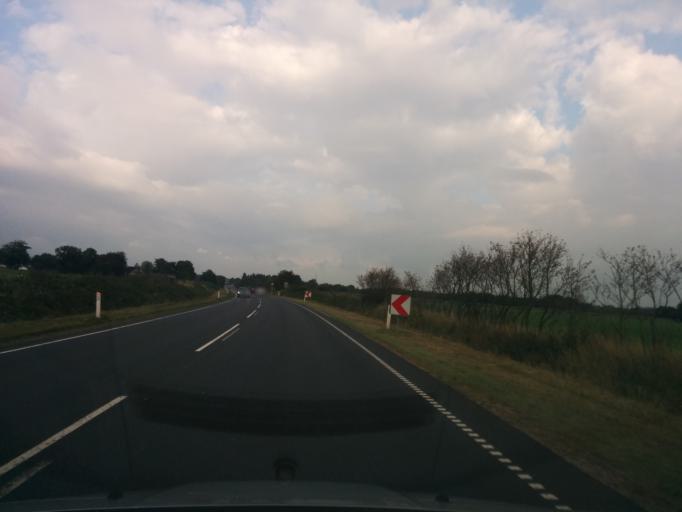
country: DK
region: South Denmark
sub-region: Billund Kommune
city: Grindsted
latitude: 55.6419
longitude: 8.8032
